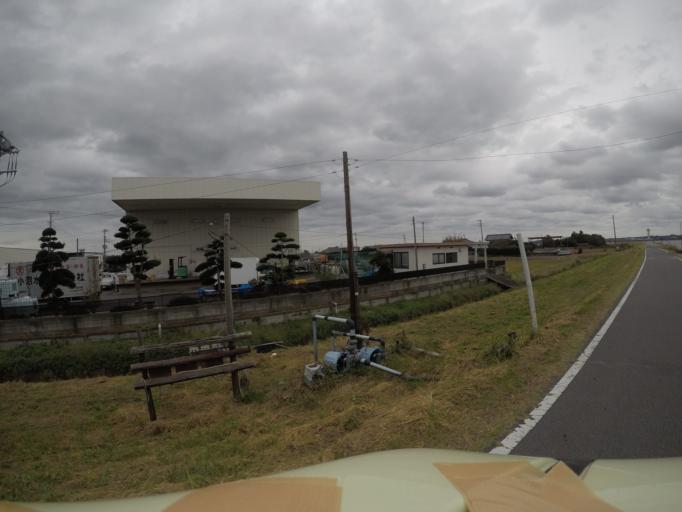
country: JP
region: Ibaraki
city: Inashiki
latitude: 36.0840
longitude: 140.3920
